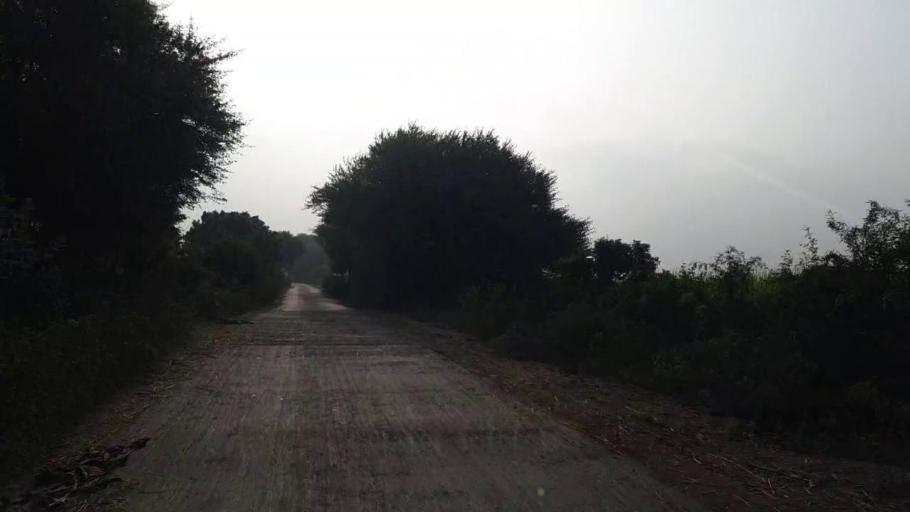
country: PK
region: Sindh
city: Tando Muhammad Khan
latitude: 25.1695
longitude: 68.6076
